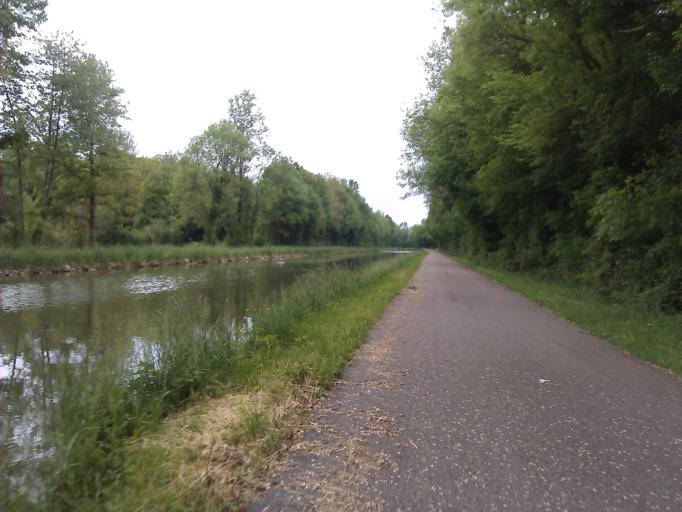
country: FR
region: Franche-Comte
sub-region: Departement du Jura
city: Damparis
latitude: 47.0797
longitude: 5.3602
